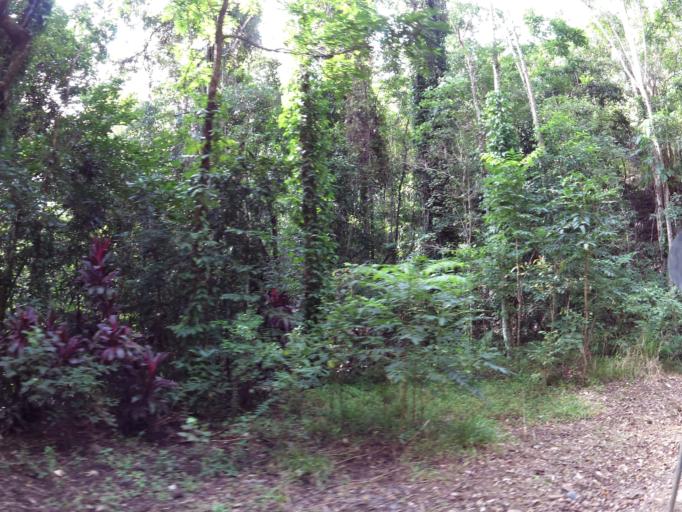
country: AU
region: Queensland
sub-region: Cairns
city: Redlynch
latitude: -16.8795
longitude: 145.6563
